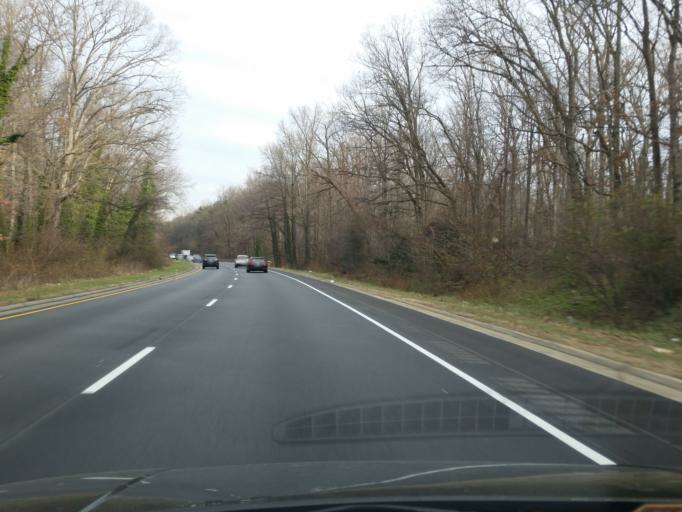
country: US
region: Maryland
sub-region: Prince George's County
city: Landover
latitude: 38.9456
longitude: -76.9091
